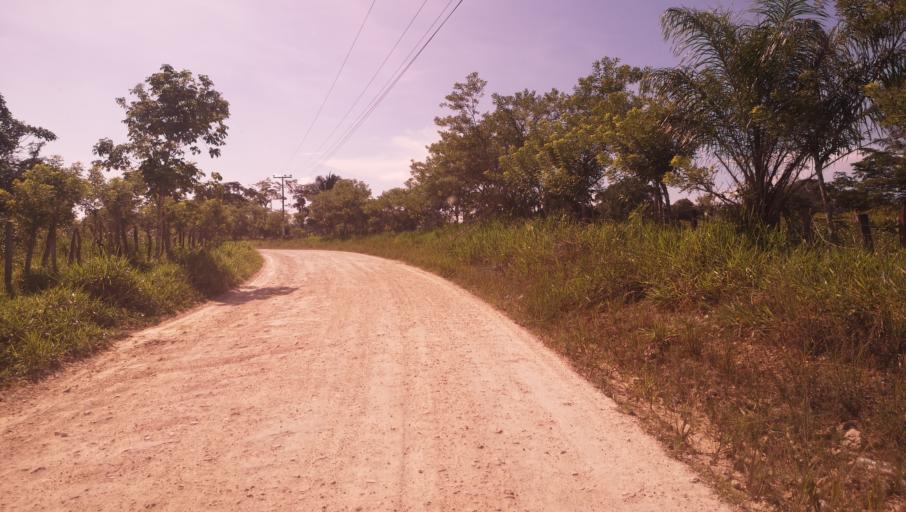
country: GT
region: Peten
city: Dolores
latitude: 16.7147
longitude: -89.3668
